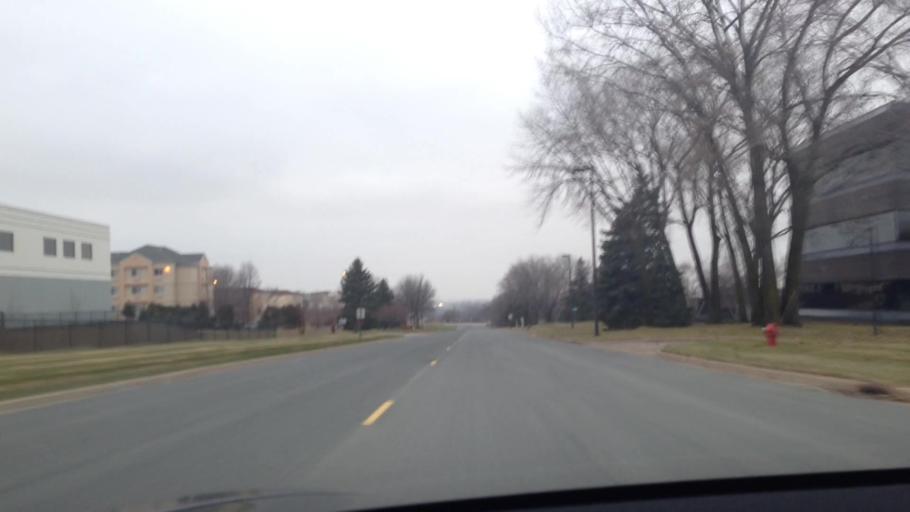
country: US
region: Minnesota
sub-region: Dakota County
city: Mendota Heights
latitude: 44.8636
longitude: -93.1606
